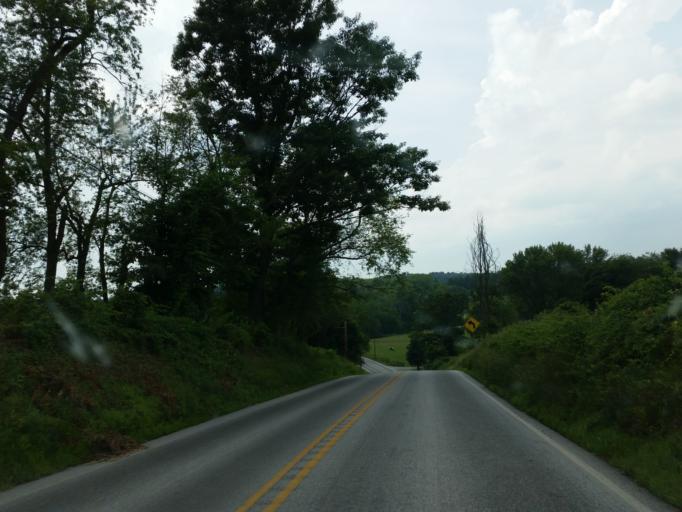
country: US
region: Pennsylvania
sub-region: Chester County
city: Oxford
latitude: 39.8681
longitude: -76.0008
